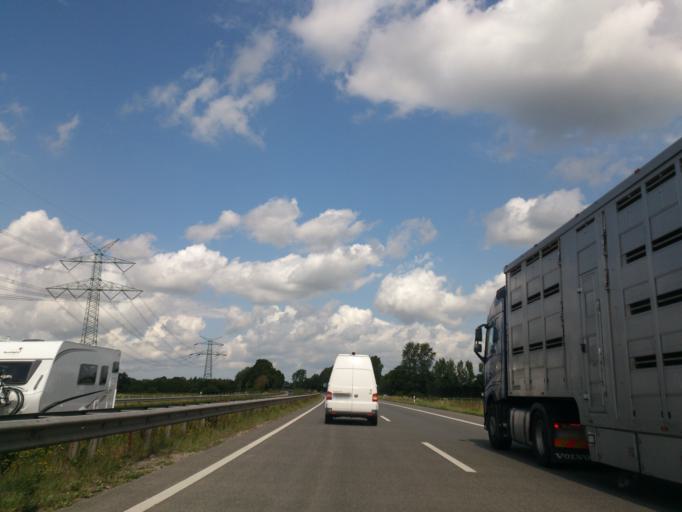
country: DE
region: Schleswig-Holstein
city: Klein Offenseth-Sparrieshoop
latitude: 53.7884
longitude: 9.7006
